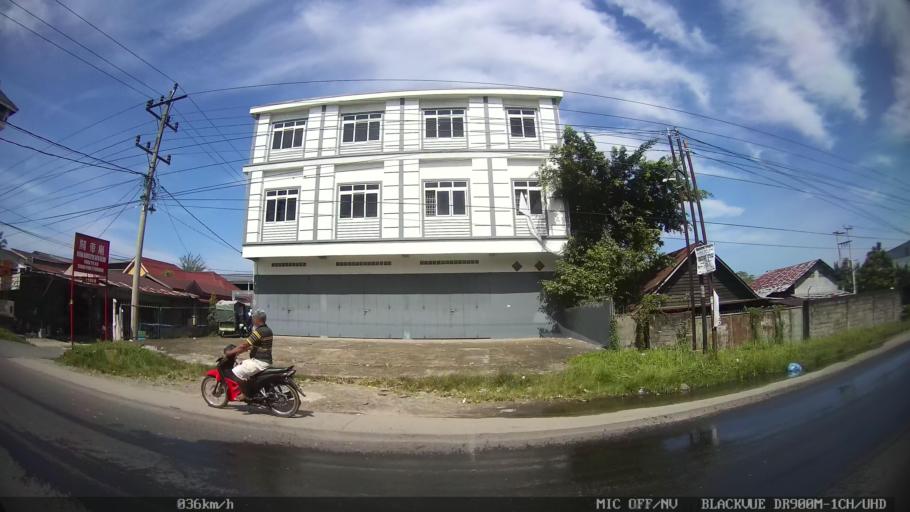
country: ID
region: North Sumatra
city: Binjai
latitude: 3.6737
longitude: 98.5093
